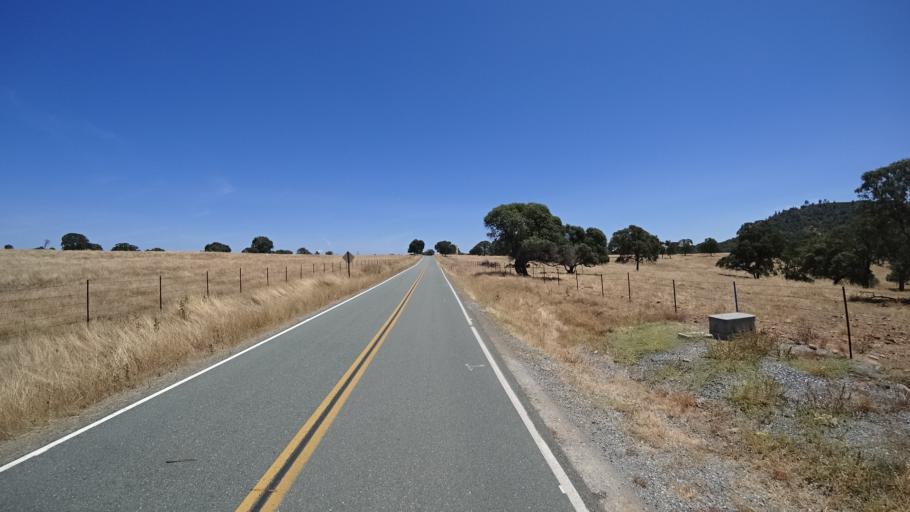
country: US
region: California
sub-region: Amador County
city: Jackson
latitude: 38.2610
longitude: -120.7513
